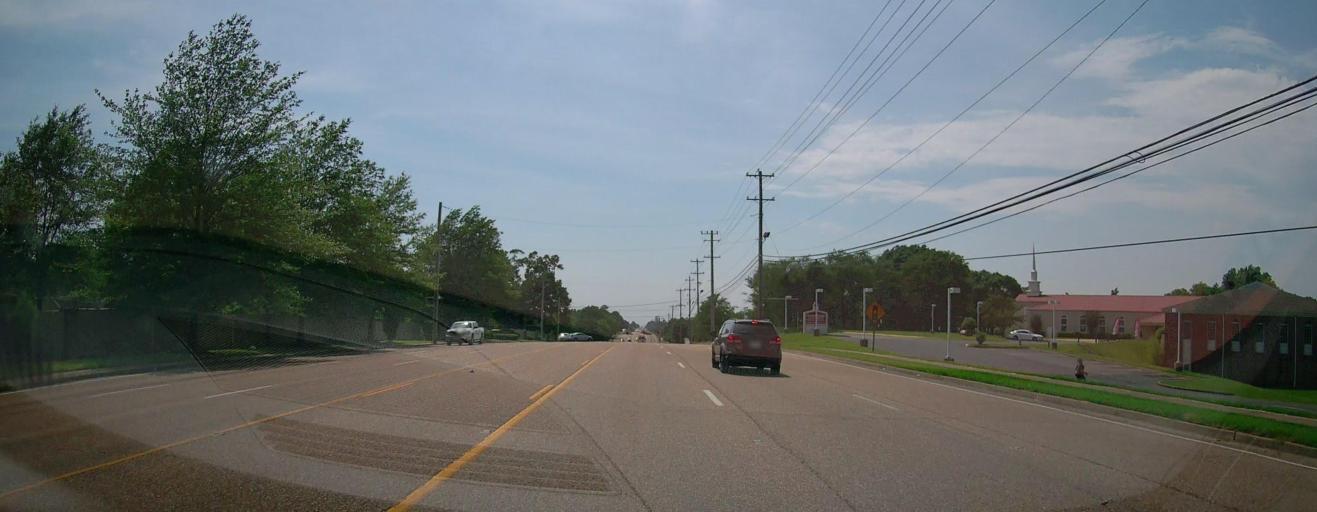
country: US
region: Mississippi
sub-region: De Soto County
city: Olive Branch
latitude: 35.0205
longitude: -89.8194
